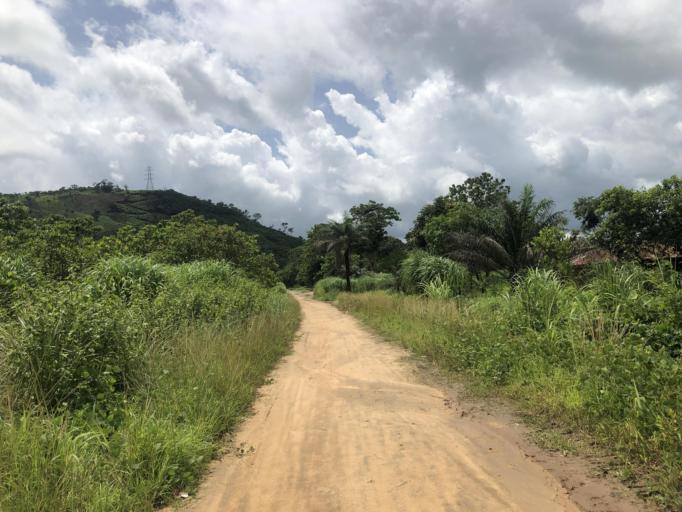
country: SL
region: Northern Province
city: Bumbuna
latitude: 9.0117
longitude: -11.7679
